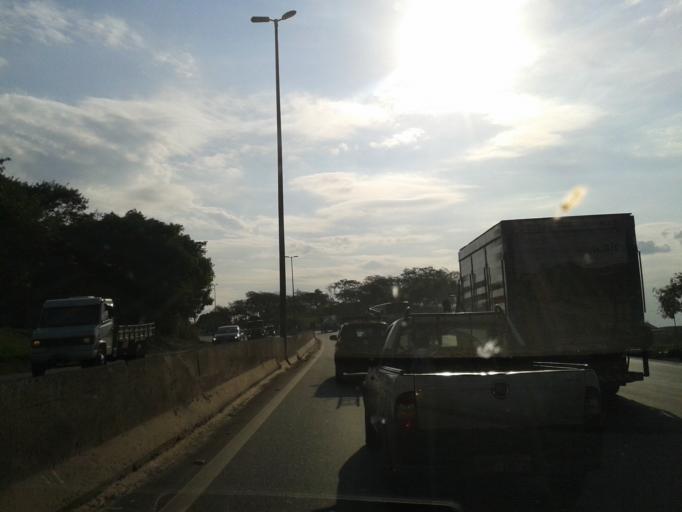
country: BR
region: Minas Gerais
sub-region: Belo Horizonte
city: Belo Horizonte
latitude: -19.8702
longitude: -43.9454
